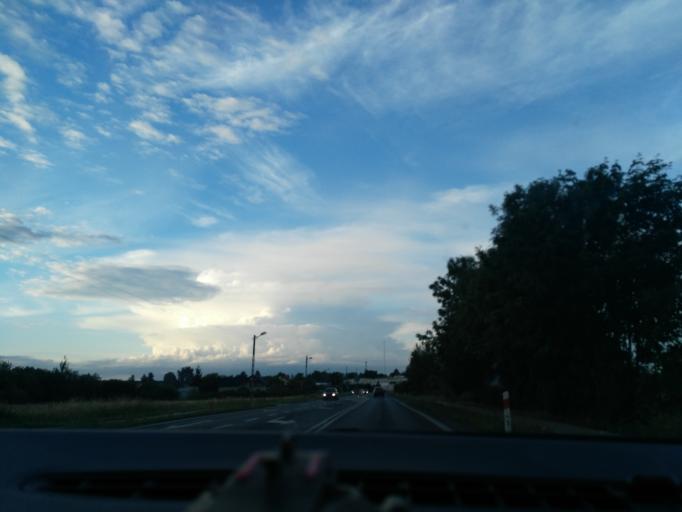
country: PL
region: Lublin Voivodeship
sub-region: Powiat lubelski
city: Niemce
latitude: 51.3616
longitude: 22.6285
